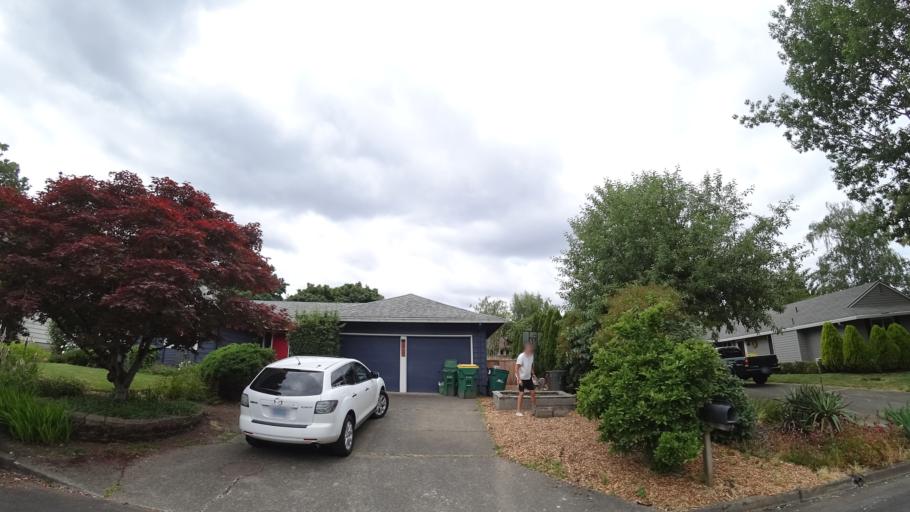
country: US
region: Oregon
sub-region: Washington County
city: Garden Home-Whitford
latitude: 45.4642
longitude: -122.7674
